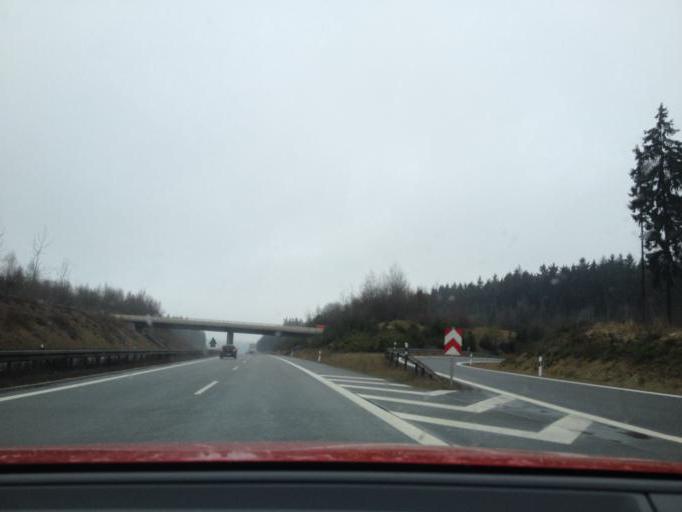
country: DE
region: Bavaria
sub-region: Upper Franconia
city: Rehau
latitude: 50.2697
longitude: 12.0305
